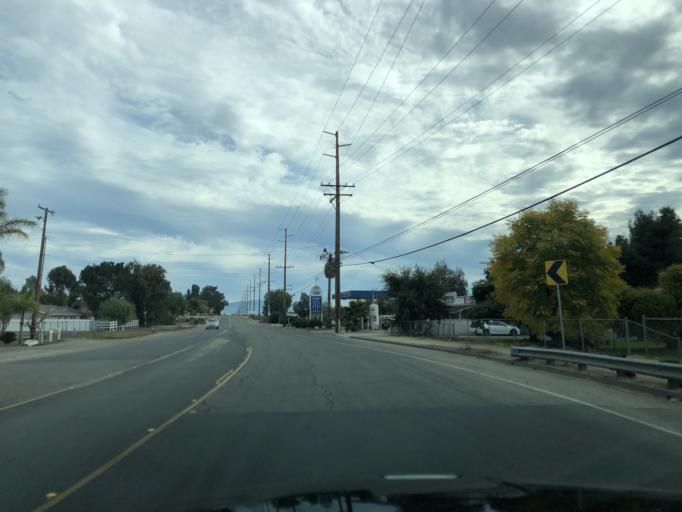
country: US
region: California
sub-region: Riverside County
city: Wildomar
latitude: 33.6141
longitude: -117.2895
